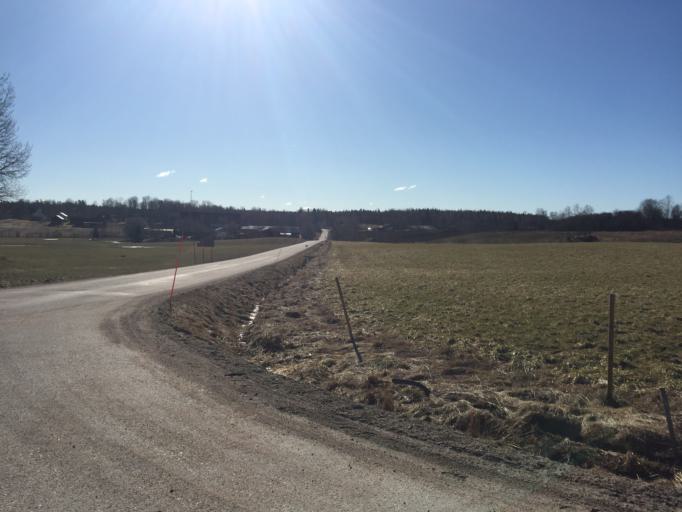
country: SE
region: OEstergoetland
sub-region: Finspangs Kommun
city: Finspang
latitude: 58.8982
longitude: 15.6910
